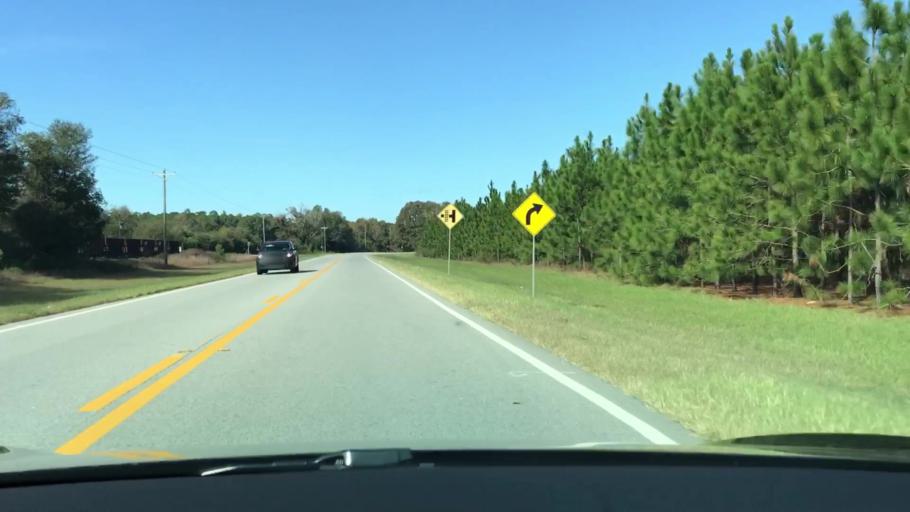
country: US
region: Georgia
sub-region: Glascock County
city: Gibson
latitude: 33.3069
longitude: -82.5297
